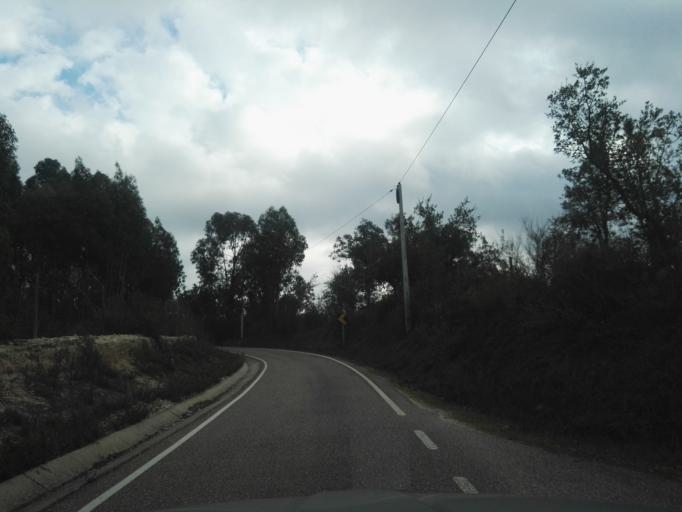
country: PT
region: Portalegre
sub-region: Nisa
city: Nisa
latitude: 39.4710
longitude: -7.7126
